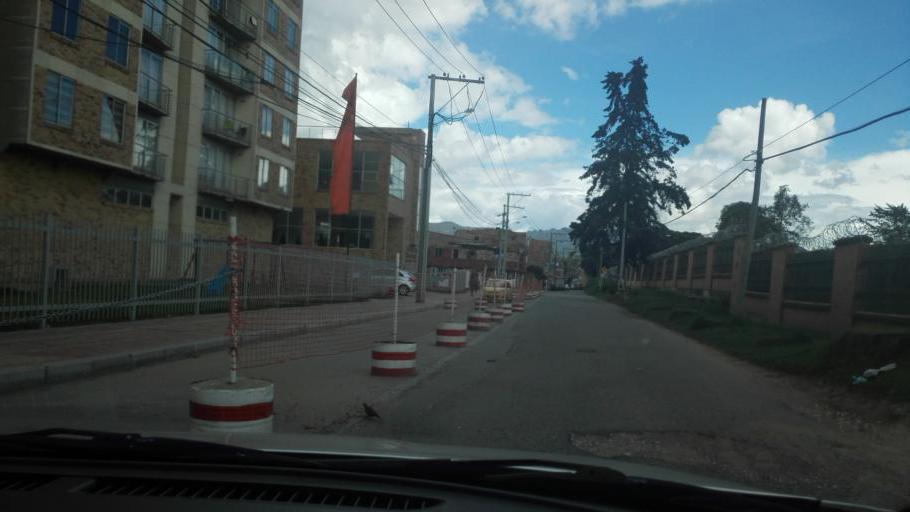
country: CO
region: Cundinamarca
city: Cota
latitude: 4.7384
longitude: -74.0700
